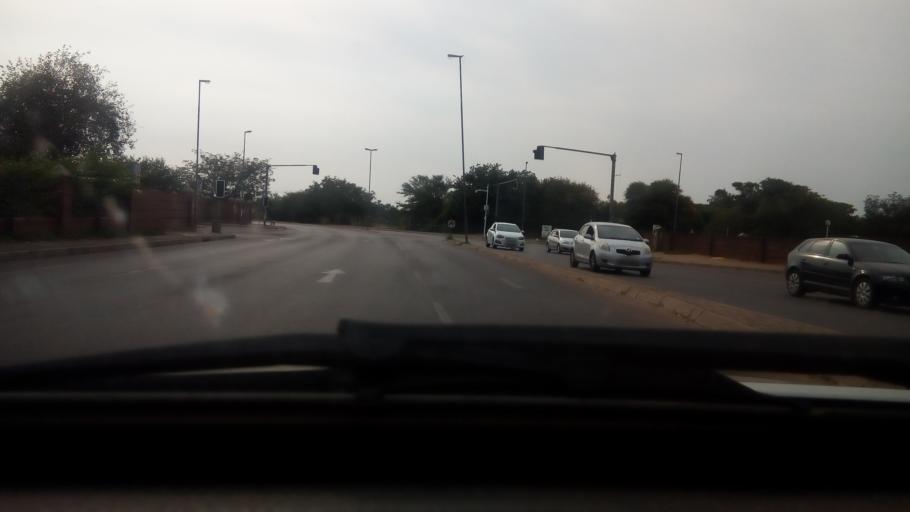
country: BW
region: South East
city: Gaborone
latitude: -24.6656
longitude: 25.9308
